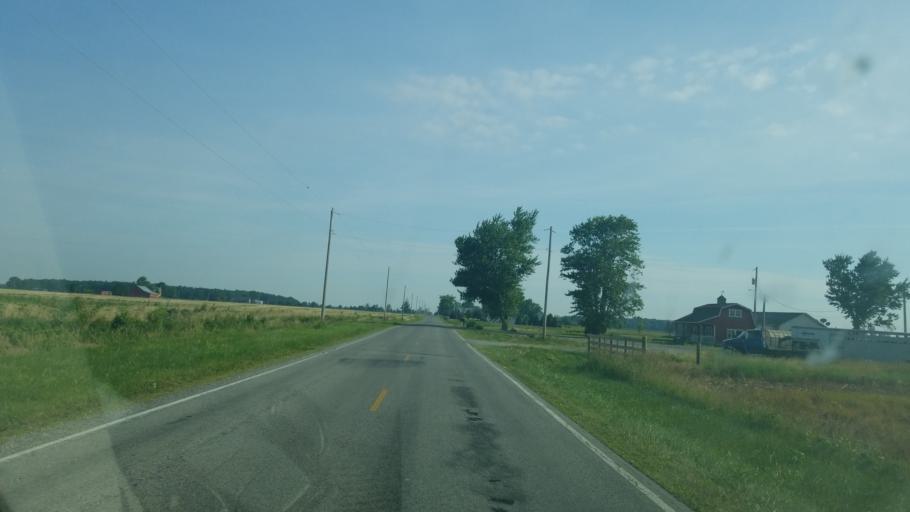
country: US
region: Ohio
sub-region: Hancock County
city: Arlington
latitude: 40.9287
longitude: -83.6988
